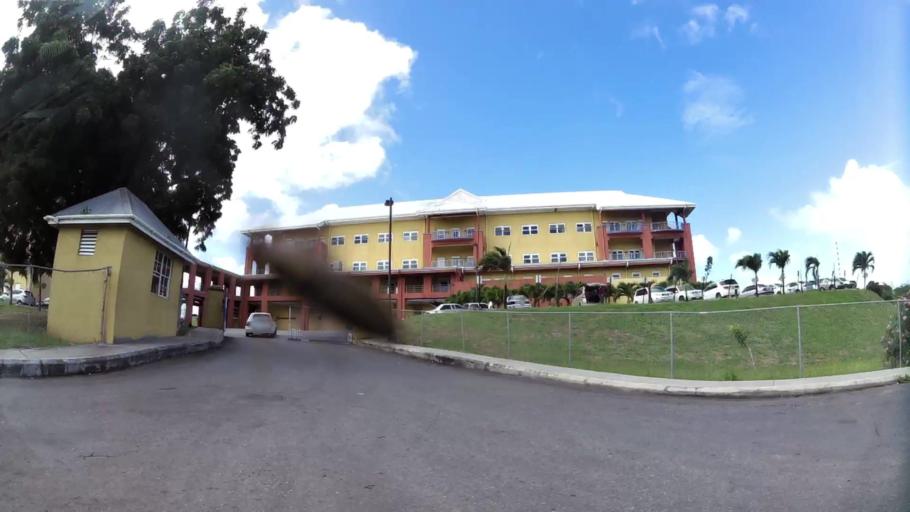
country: AG
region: Saint John
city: Saint John's
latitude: 17.1166
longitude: -61.8381
